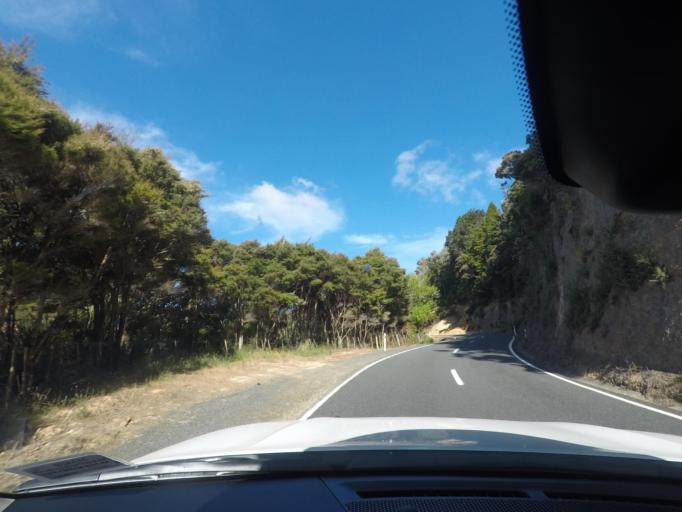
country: NZ
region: Northland
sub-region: Whangarei
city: Ngunguru
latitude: -35.6714
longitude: 174.4620
